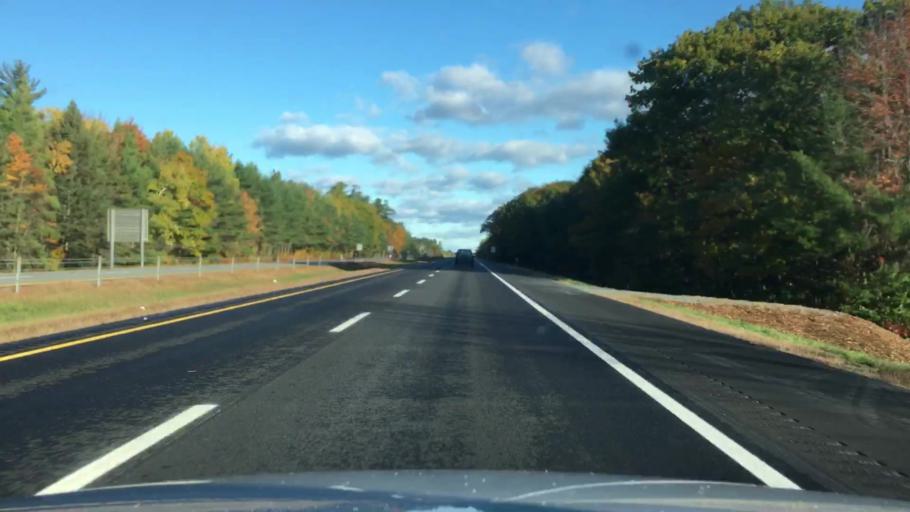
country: US
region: Maine
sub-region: Penobscot County
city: Orono
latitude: 44.9100
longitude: -68.6955
